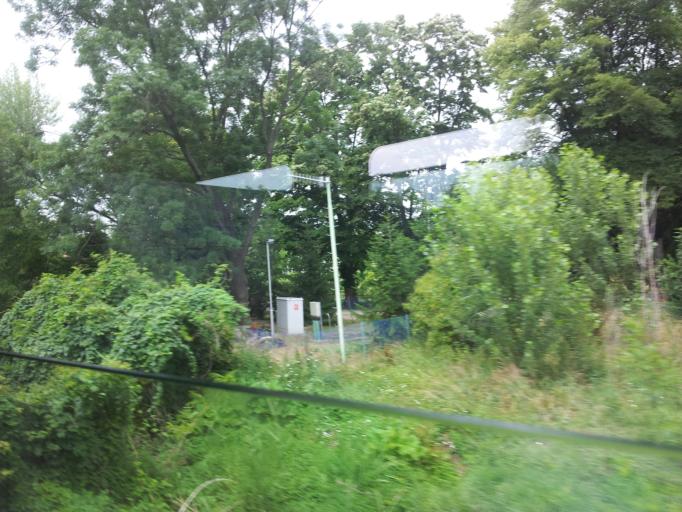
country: HU
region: Veszprem
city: Badacsonytomaj
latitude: 46.7892
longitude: 17.4781
